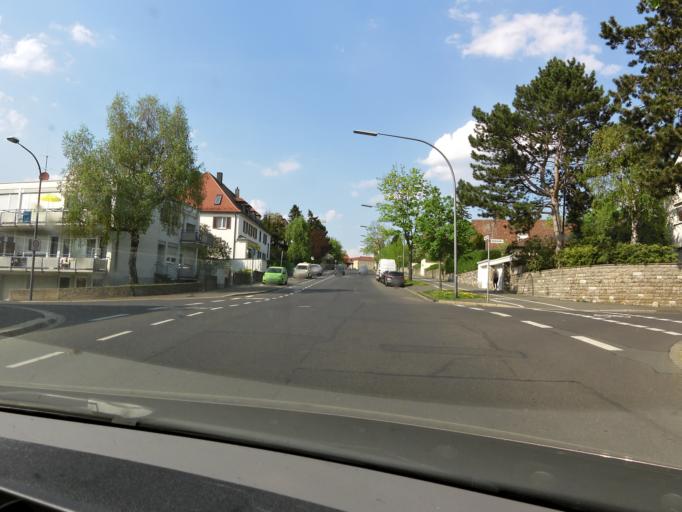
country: DE
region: Bavaria
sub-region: Regierungsbezirk Unterfranken
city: Wuerzburg
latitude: 49.7893
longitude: 9.9530
